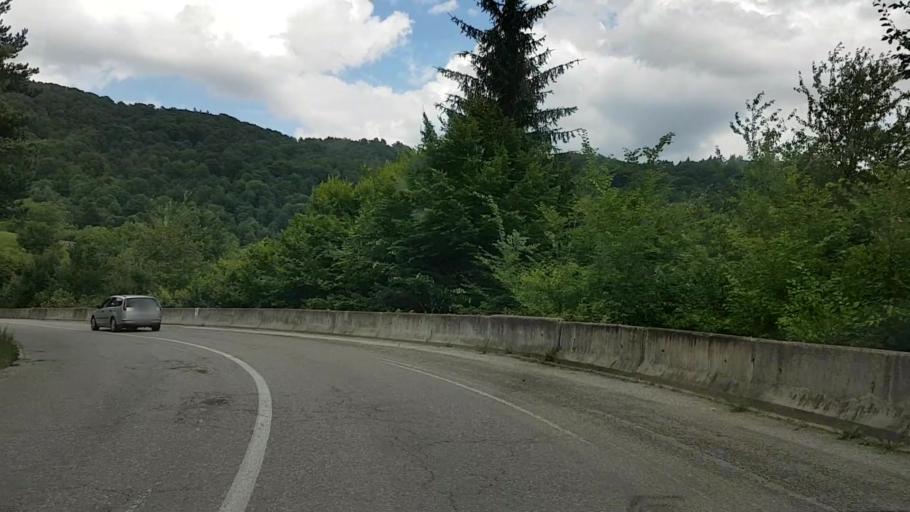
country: RO
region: Neamt
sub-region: Comuna Pangarati
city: Pangarati
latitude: 46.9502
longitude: 26.1264
